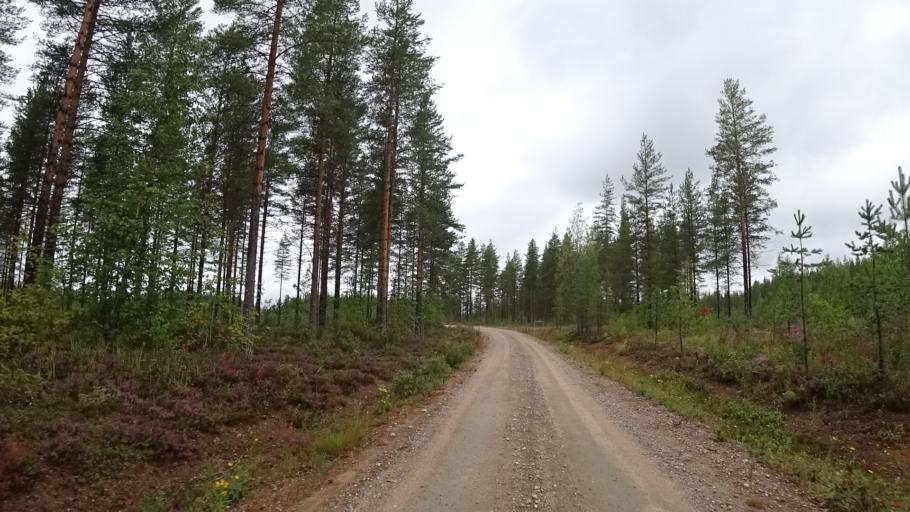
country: FI
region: North Karelia
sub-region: Pielisen Karjala
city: Lieksa
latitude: 63.5187
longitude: 30.1130
